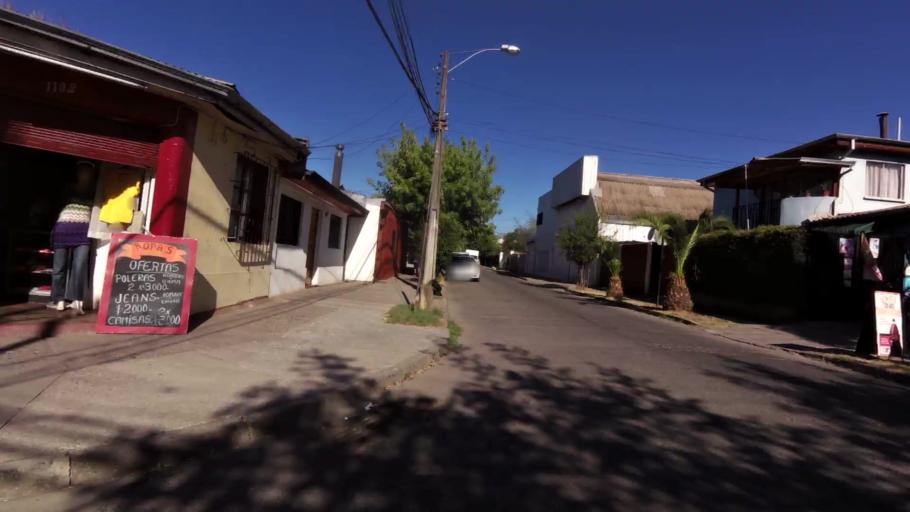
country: CL
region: O'Higgins
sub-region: Provincia de Colchagua
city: Chimbarongo
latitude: -34.5792
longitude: -70.9944
